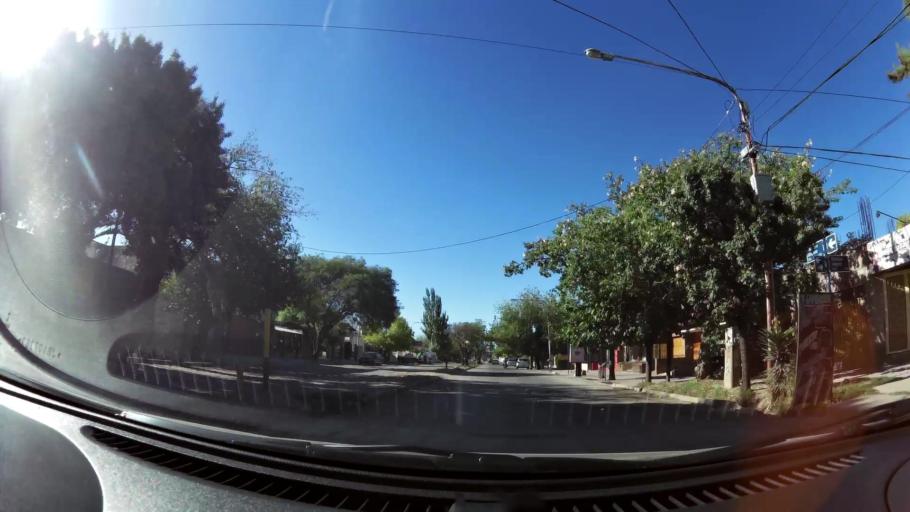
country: AR
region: Mendoza
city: Las Heras
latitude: -32.8603
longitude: -68.8215
